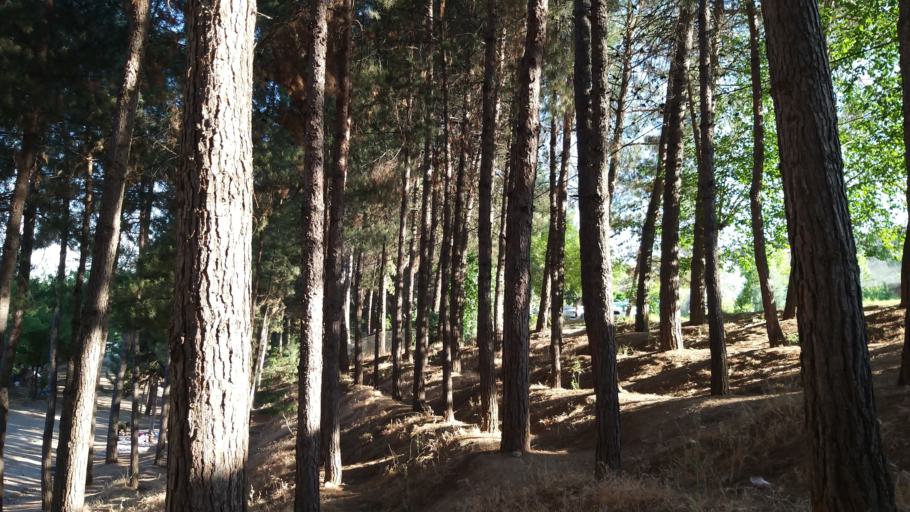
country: TR
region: Diyarbakir
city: Malabadi
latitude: 38.1551
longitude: 41.2016
